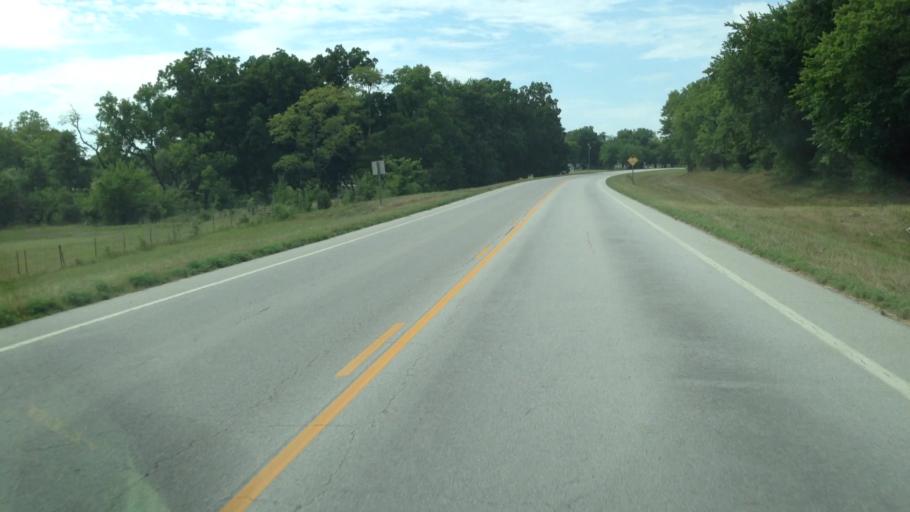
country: US
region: Kansas
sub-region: Labette County
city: Oswego
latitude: 37.1530
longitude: -95.1071
